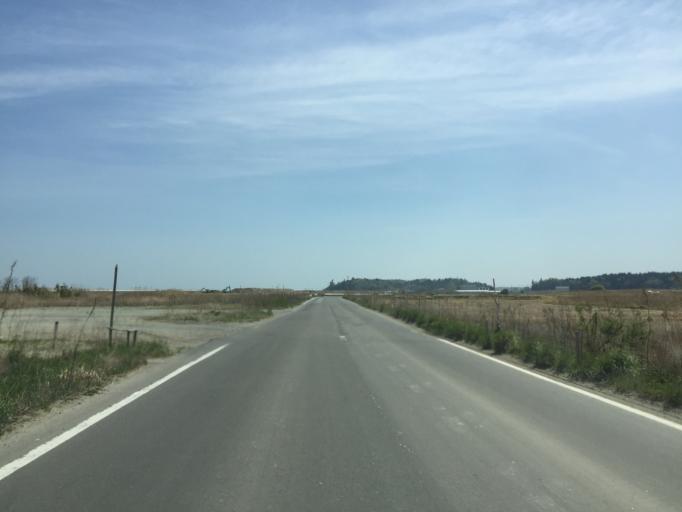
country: JP
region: Miyagi
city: Watari
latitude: 37.9106
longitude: 140.9201
